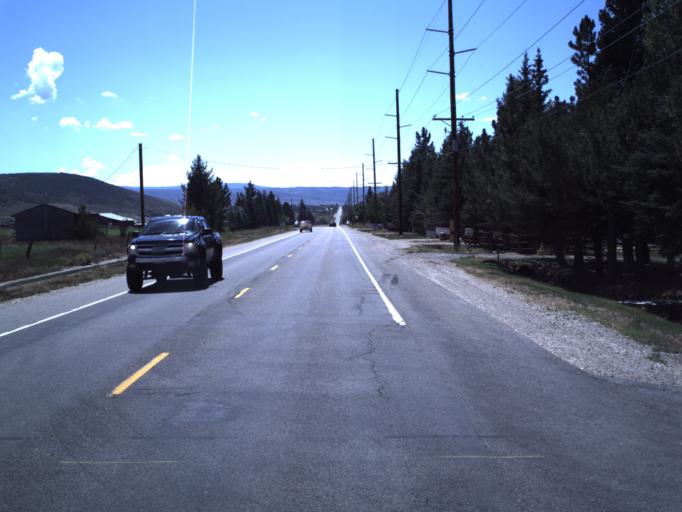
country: US
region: Utah
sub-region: Summit County
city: Kamas
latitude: 40.6804
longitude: -111.2810
